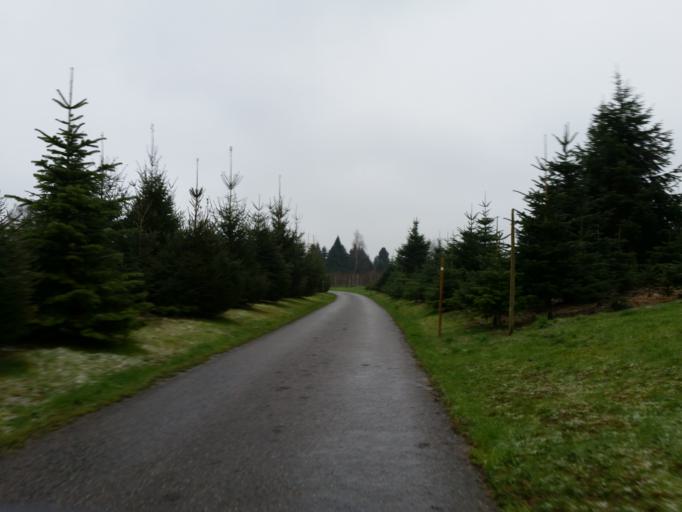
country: CH
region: Thurgau
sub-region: Arbon District
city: Egnach
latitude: 47.5311
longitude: 9.3830
